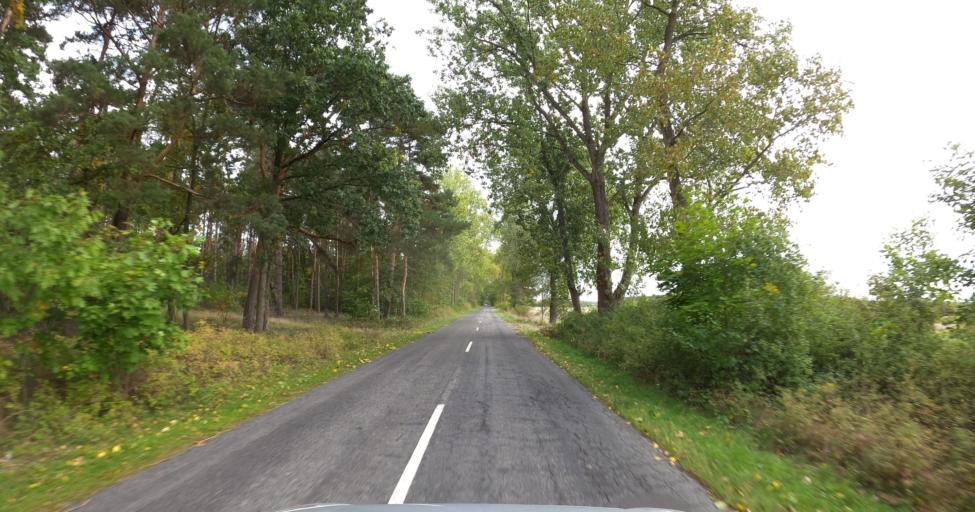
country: PL
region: Lubusz
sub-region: Powiat zielonogorski
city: Zabor
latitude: 51.9467
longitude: 15.6603
